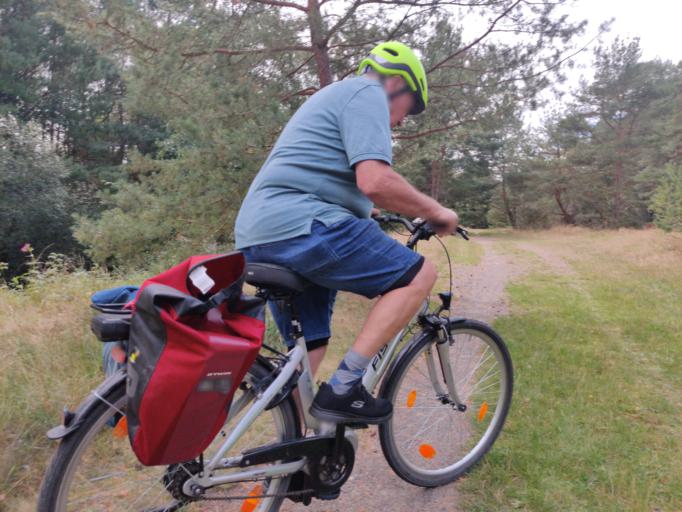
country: DE
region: Lower Saxony
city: Langelsheim
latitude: 51.9594
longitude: 10.3543
